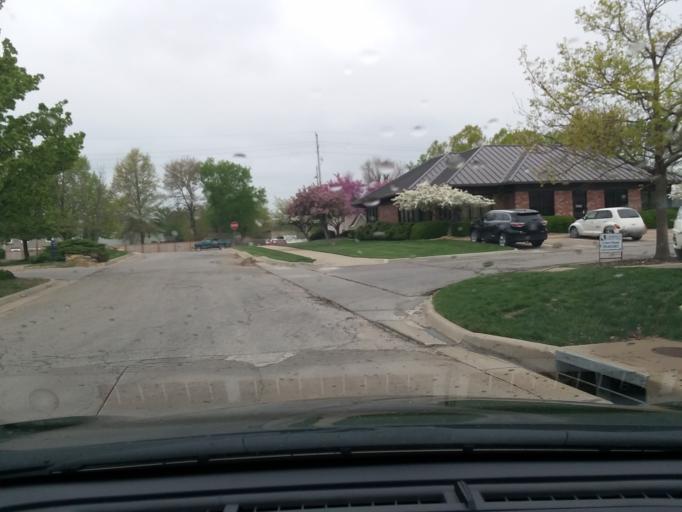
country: US
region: Kansas
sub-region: Douglas County
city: Lawrence
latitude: 38.9723
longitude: -95.2917
